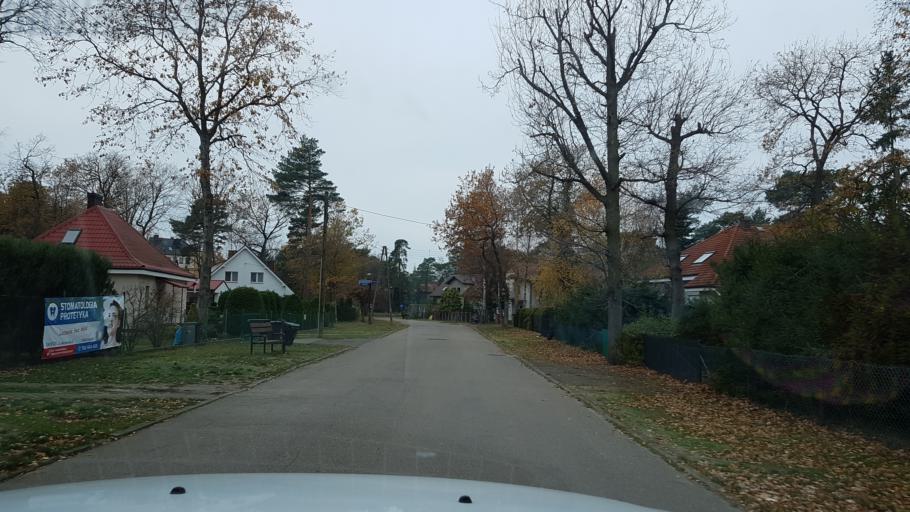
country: PL
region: West Pomeranian Voivodeship
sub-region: Powiat gryficki
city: Pobierowo
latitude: 54.0599
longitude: 14.9381
